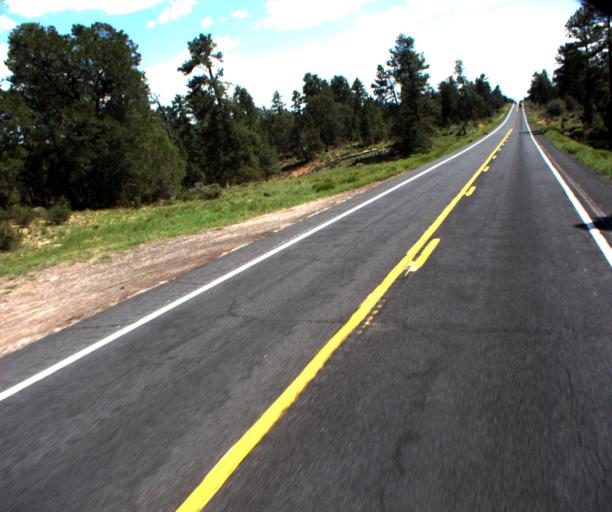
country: US
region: Arizona
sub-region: Coconino County
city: Grand Canyon Village
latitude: 35.8739
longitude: -112.1326
